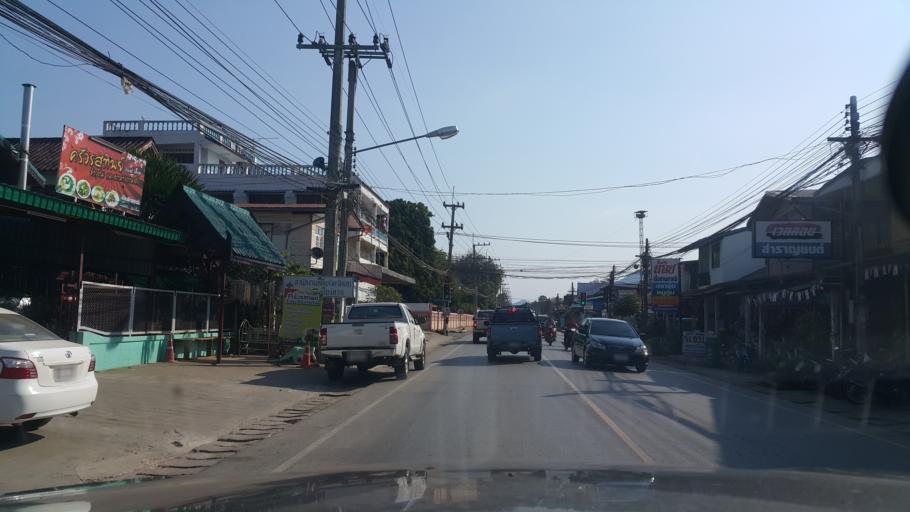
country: TH
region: Loei
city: Chiang Khan
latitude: 17.8954
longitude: 101.6604
